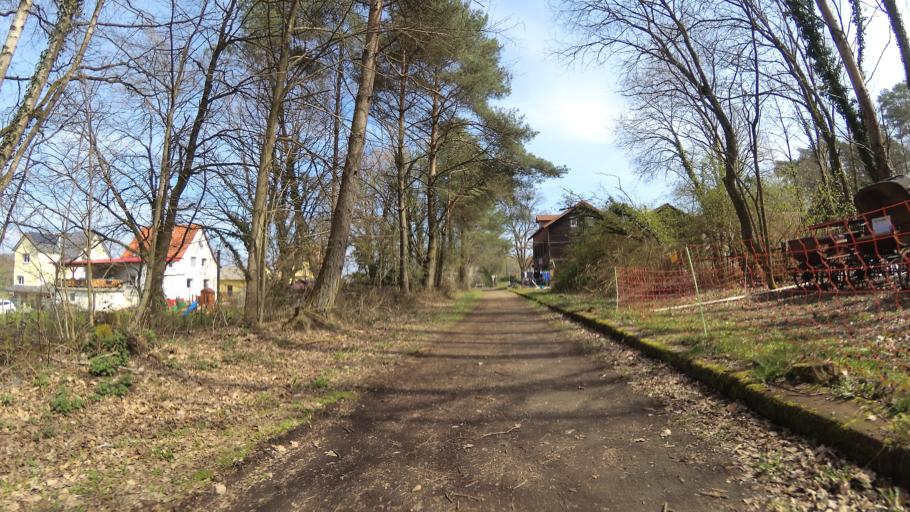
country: DE
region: Rheinland-Pfalz
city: Gries
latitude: 49.4120
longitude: 7.4159
